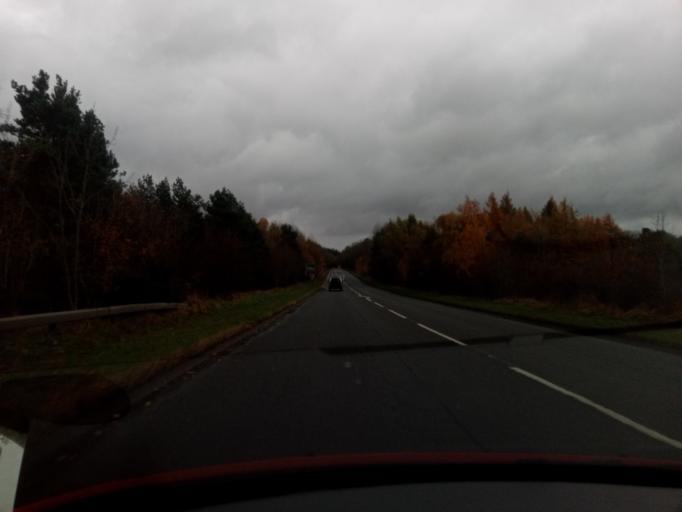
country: GB
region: England
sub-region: County Durham
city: High Etherley
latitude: 54.6728
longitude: -1.7775
